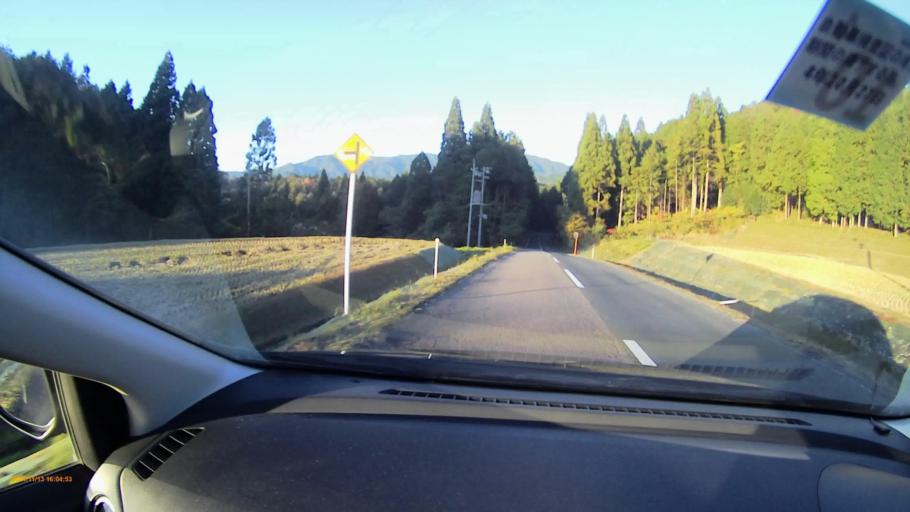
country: JP
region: Gifu
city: Nakatsugawa
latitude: 35.5957
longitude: 137.4698
